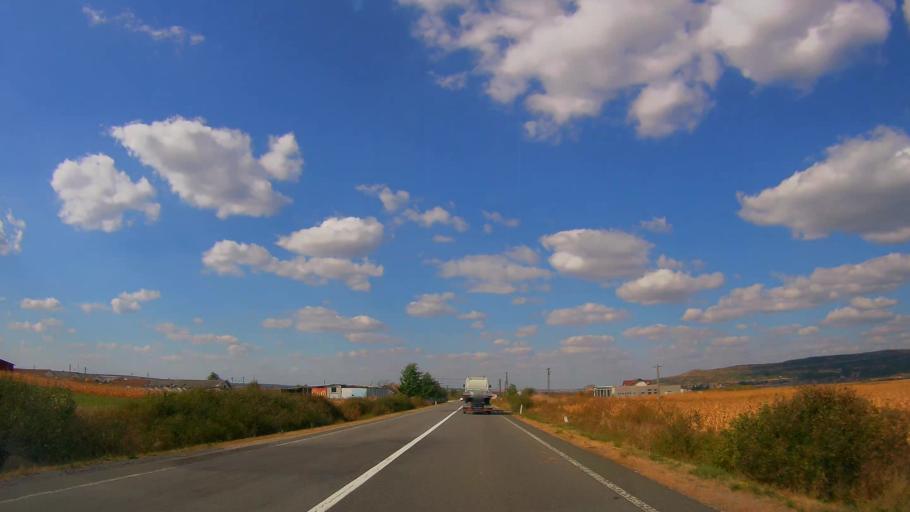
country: RO
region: Salaj
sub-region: Comuna Bobota
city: Dersida
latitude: 47.3634
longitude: 22.7934
